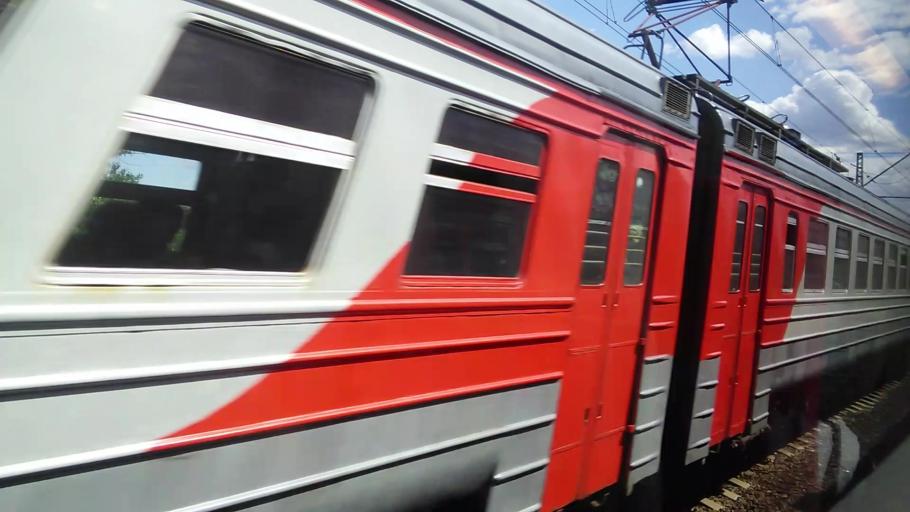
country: RU
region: Moscow
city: Likhobory
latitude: 55.8500
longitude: 37.5732
